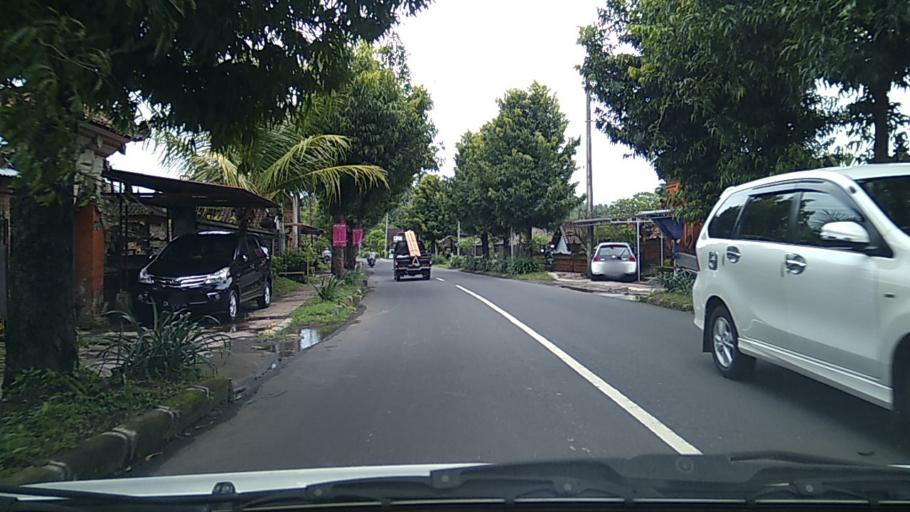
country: ID
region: Bali
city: Banjar Kelodan
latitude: -8.5333
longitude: 115.3485
